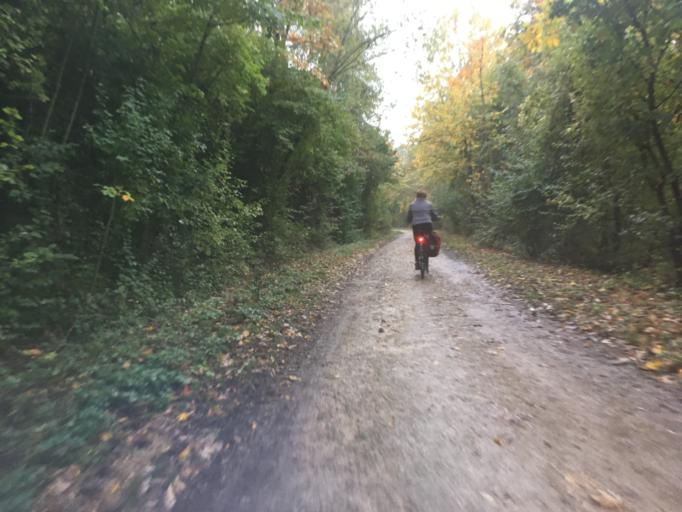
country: DE
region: Baden-Wuerttemberg
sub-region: Tuebingen Region
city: Nehren
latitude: 48.4172
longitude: 9.0737
